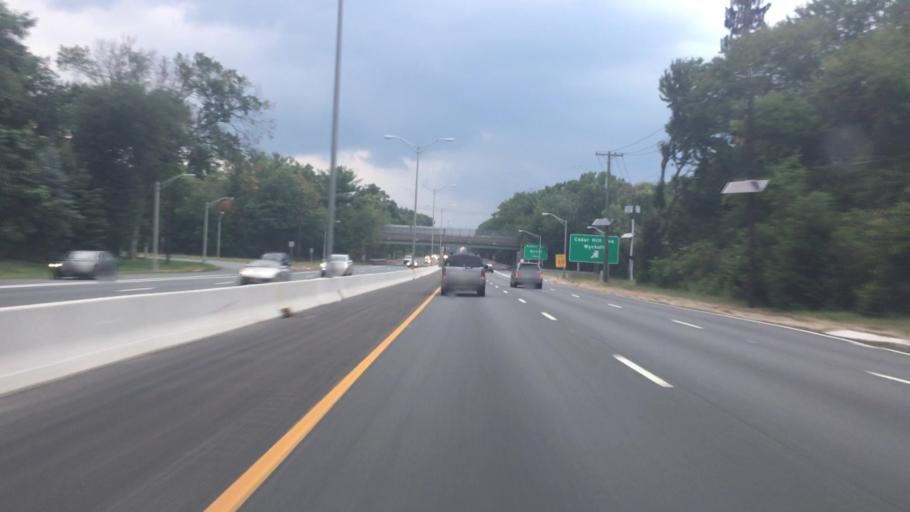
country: US
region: New Jersey
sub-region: Bergen County
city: Wyckoff
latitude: 40.9858
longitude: -74.1661
